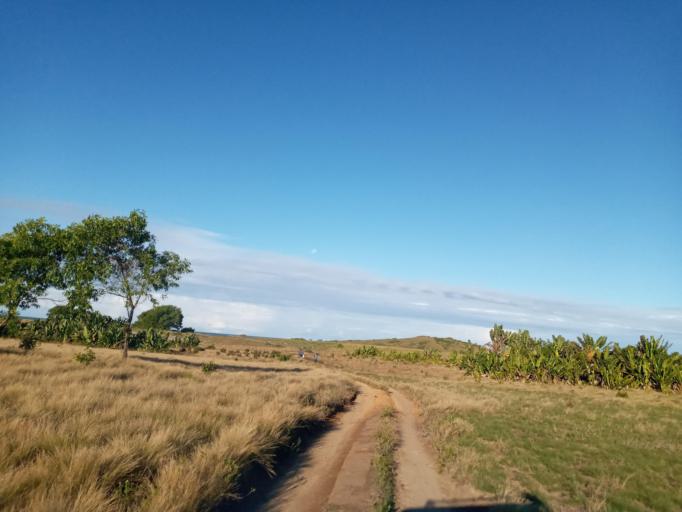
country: MG
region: Anosy
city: Fort Dauphin
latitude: -24.4313
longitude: 47.2979
